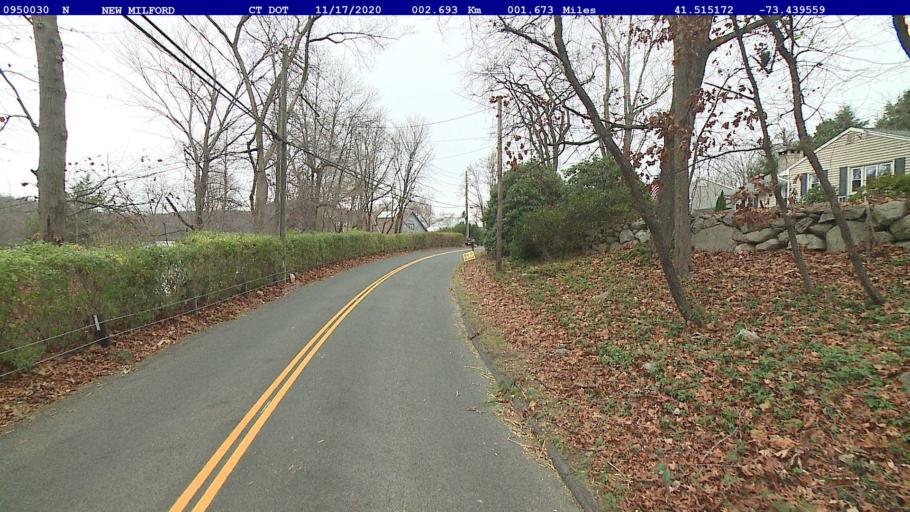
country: US
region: Connecticut
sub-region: Litchfield County
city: New Milford
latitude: 41.5152
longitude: -73.4397
